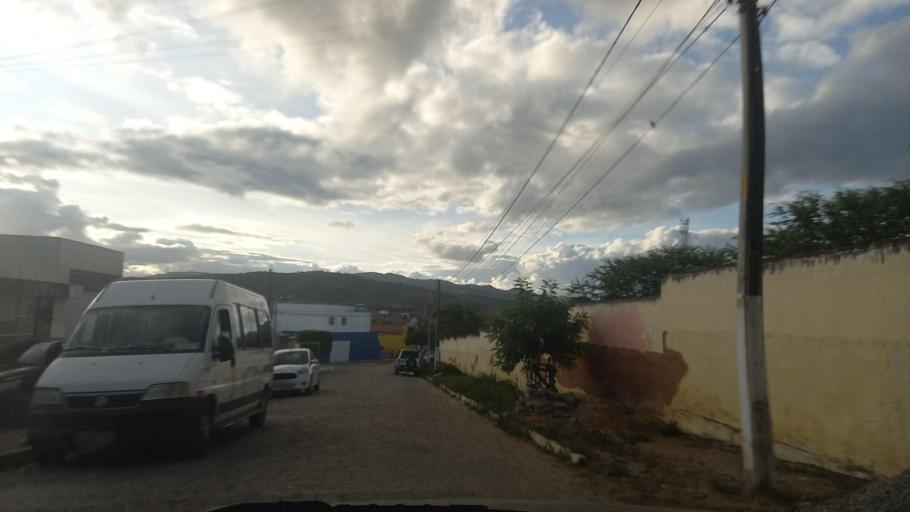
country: BR
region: Pernambuco
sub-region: Bezerros
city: Bezerros
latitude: -8.2375
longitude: -35.7487
